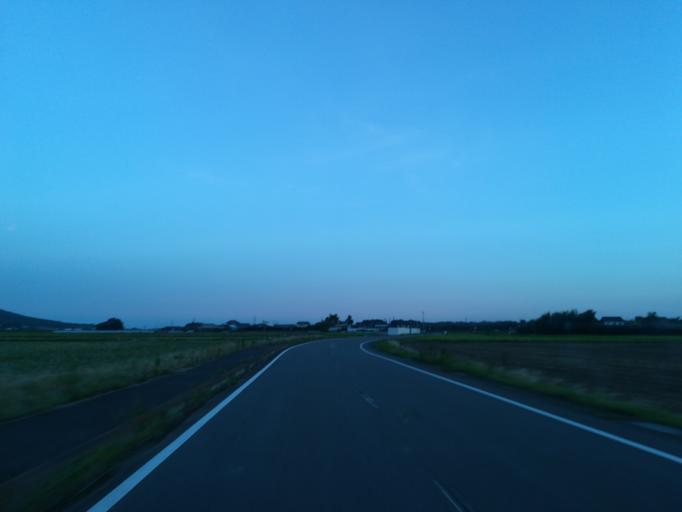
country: JP
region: Ibaraki
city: Makabe
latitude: 36.2483
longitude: 140.0570
